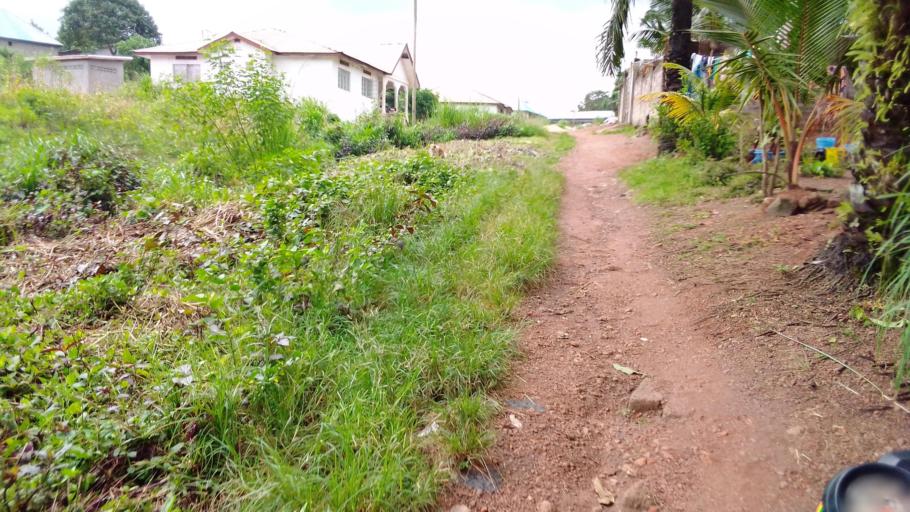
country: SL
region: Eastern Province
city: Kenema
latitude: 7.8713
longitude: -11.1751
